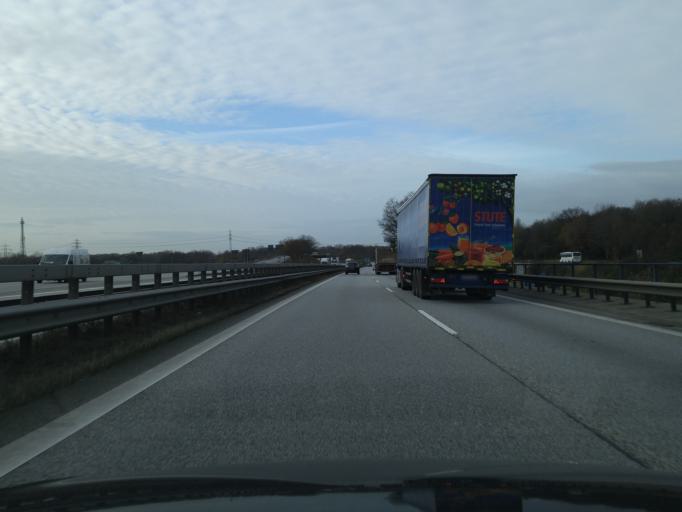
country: DE
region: Schleswig-Holstein
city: Barsbuettel
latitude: 53.5616
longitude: 10.1712
